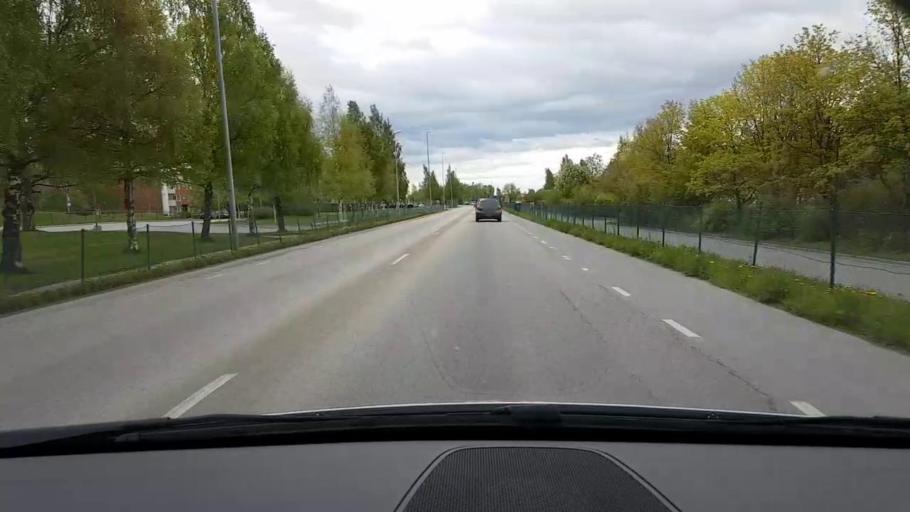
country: SE
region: Jaemtland
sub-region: OEstersunds Kommun
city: Ostersund
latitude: 63.1567
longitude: 14.6776
